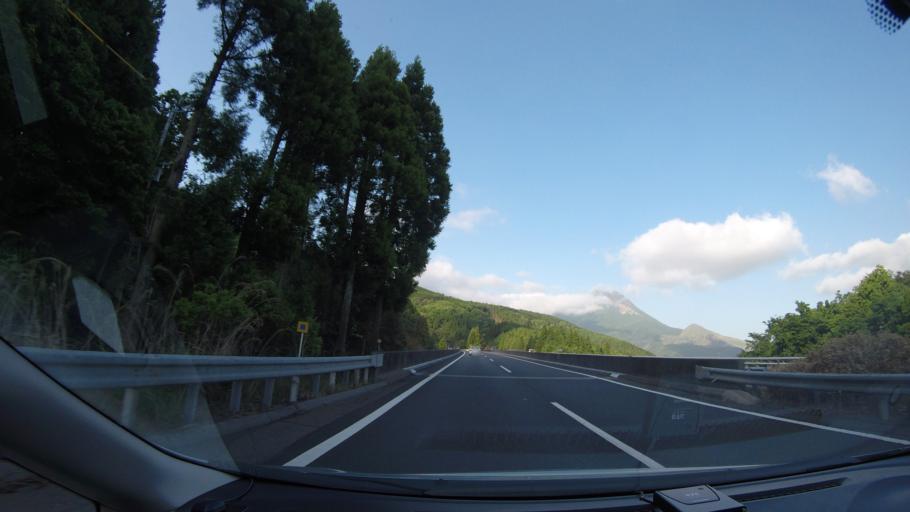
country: JP
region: Oita
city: Beppu
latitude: 33.2652
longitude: 131.3360
